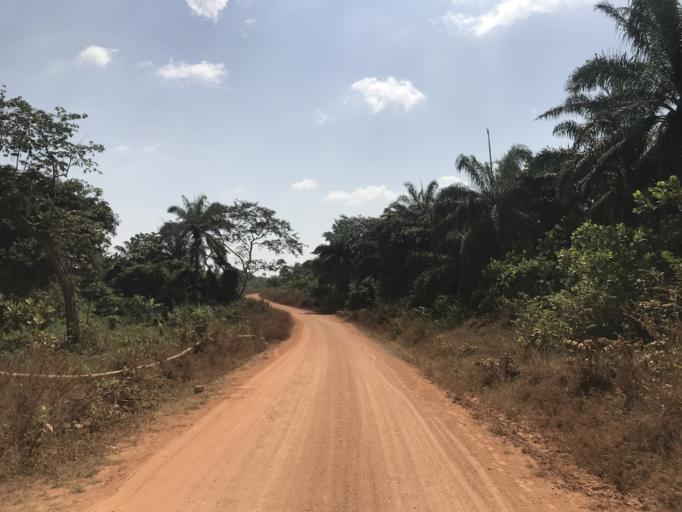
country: NG
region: Osun
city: Ifon
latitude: 7.9066
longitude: 4.4792
